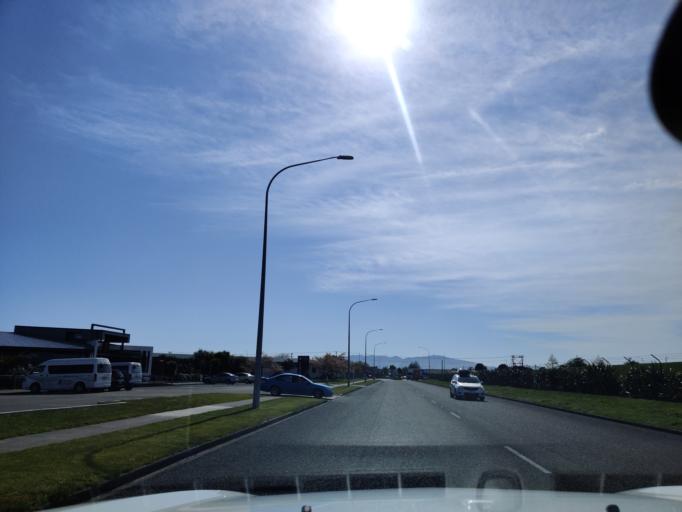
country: NZ
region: Manawatu-Wanganui
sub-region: Palmerston North City
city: Palmerston North
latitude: -40.3316
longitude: 175.6500
